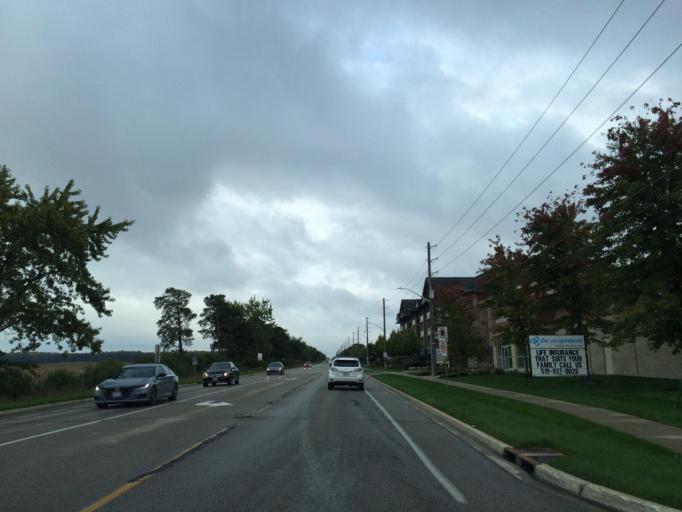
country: CA
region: Ontario
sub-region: Wellington County
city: Guelph
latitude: 43.5240
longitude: -80.1856
